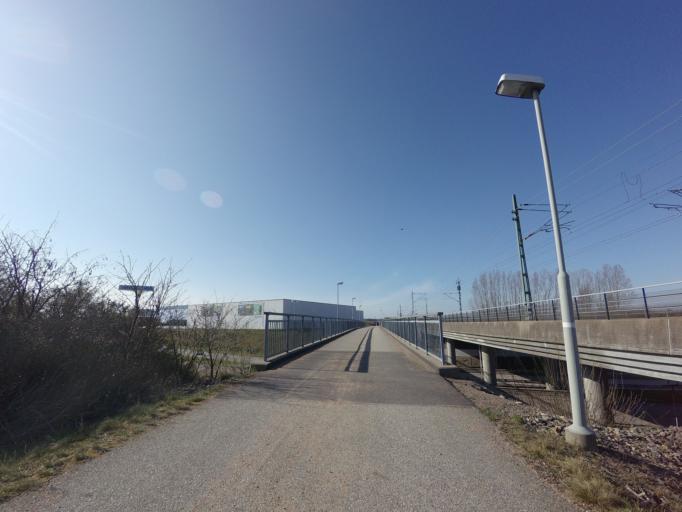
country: SE
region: Skane
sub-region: Landskrona
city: Landskrona
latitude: 55.8727
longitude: 12.8627
